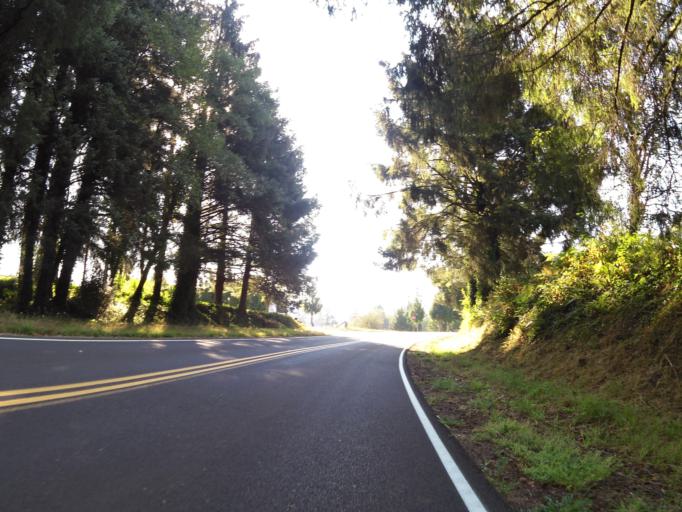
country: US
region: Oregon
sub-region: Tillamook County
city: Tillamook
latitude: 45.4008
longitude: -123.7934
